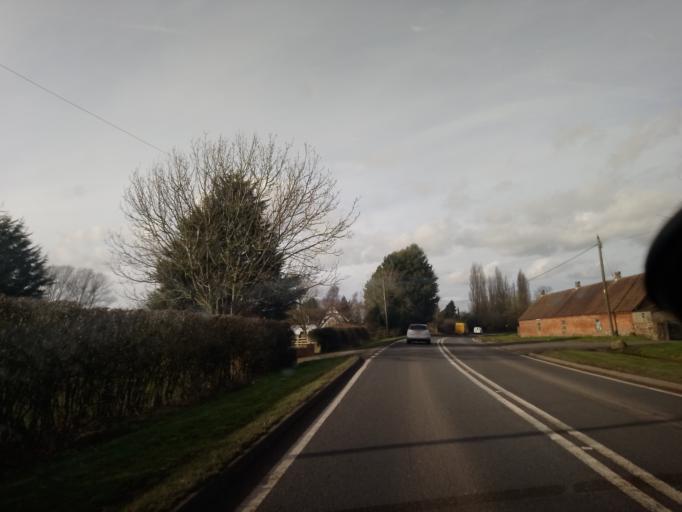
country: GB
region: England
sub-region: Telford and Wrekin
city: Eyton upon the Weald Moors
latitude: 52.7537
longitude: -2.5473
